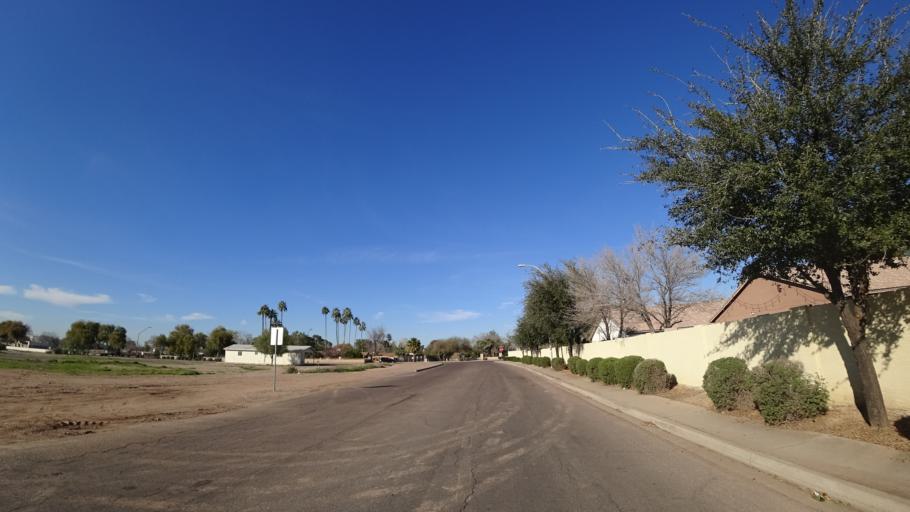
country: US
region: Arizona
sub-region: Maricopa County
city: Glendale
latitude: 33.5224
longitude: -112.2290
